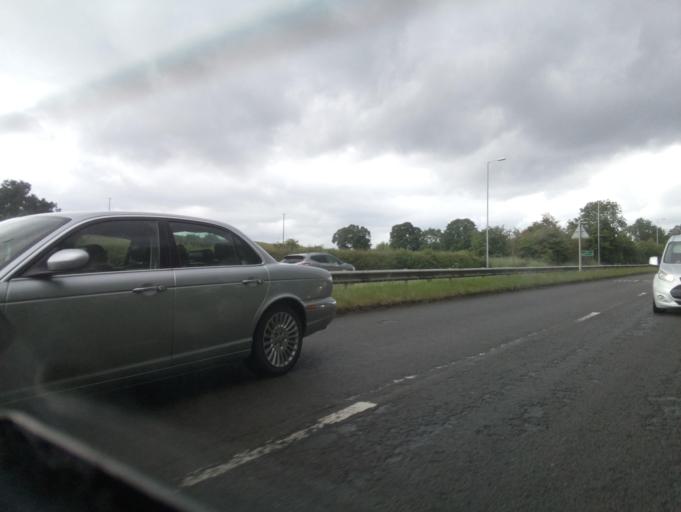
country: GB
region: England
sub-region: Dudley
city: Kingswinford
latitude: 52.5421
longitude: -2.1754
